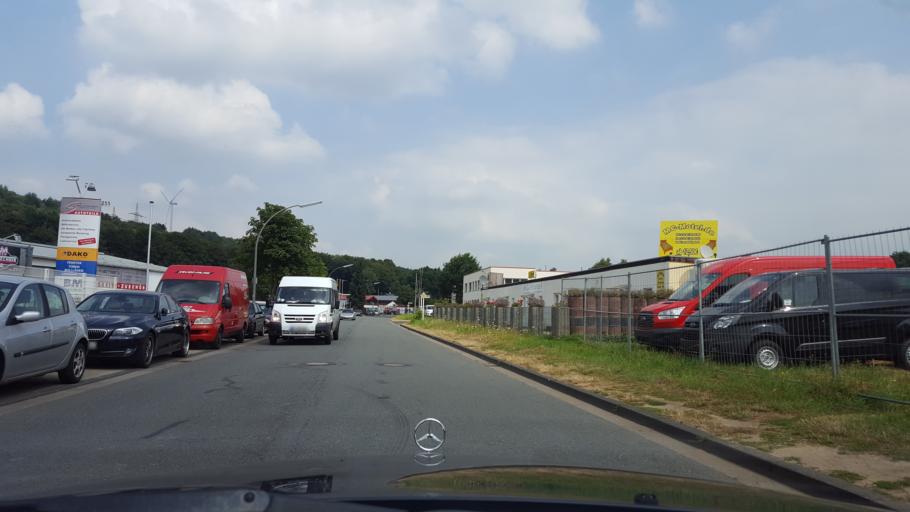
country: DE
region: North Rhine-Westphalia
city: Marl
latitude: 51.6712
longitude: 7.1541
